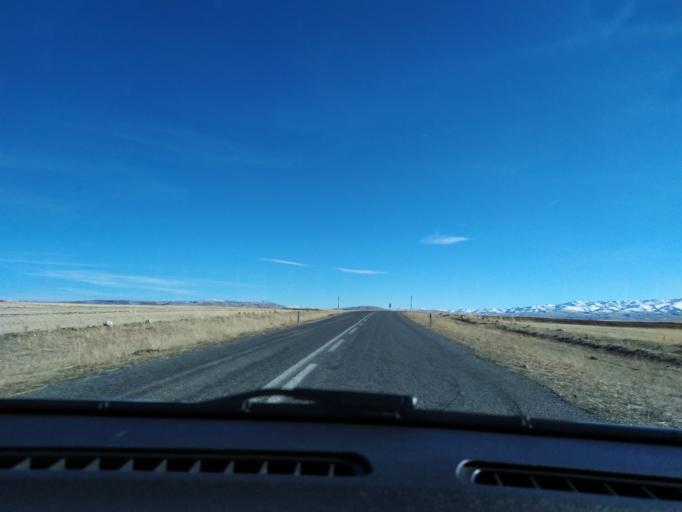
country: TR
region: Kayseri
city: Orensehir
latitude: 38.9487
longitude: 36.6955
